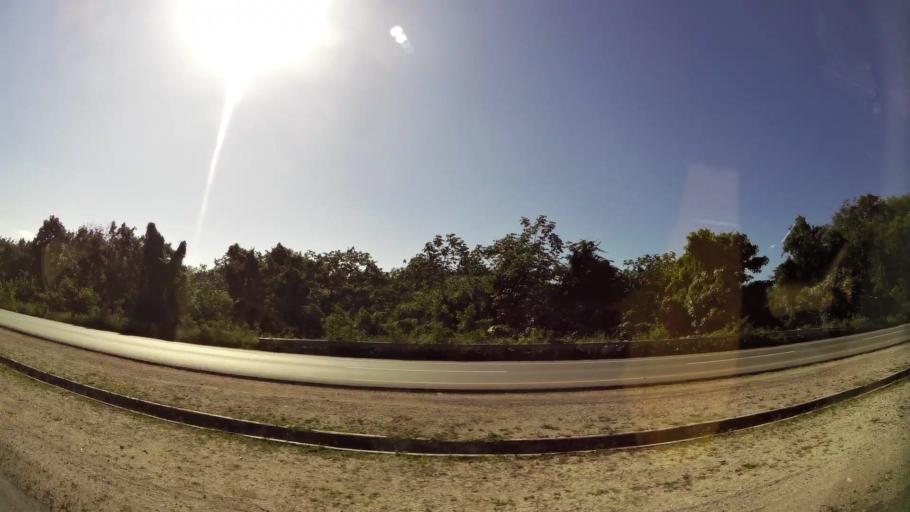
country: DO
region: San Cristobal
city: El Carril
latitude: 18.4359
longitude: -70.0263
